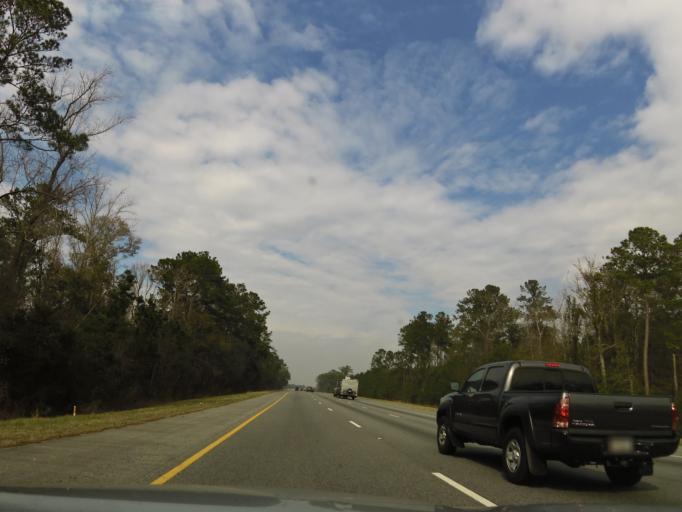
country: US
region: Georgia
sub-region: Liberty County
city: Midway
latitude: 31.7219
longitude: -81.3886
